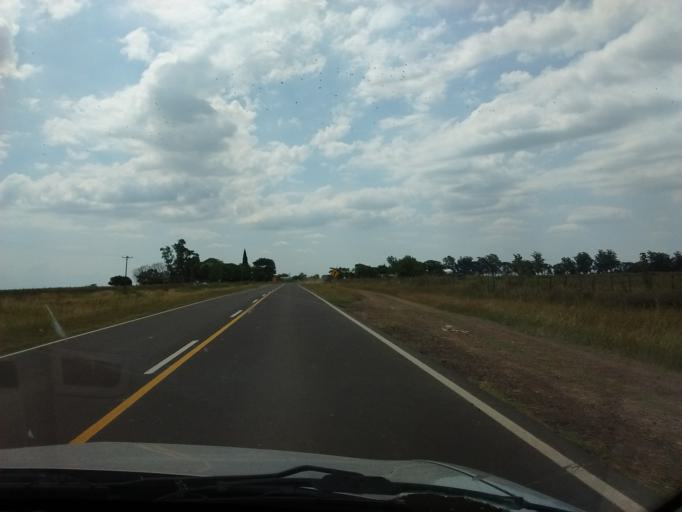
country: AR
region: Entre Rios
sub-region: Departamento de Victoria
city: Victoria
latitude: -32.7697
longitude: -59.9239
